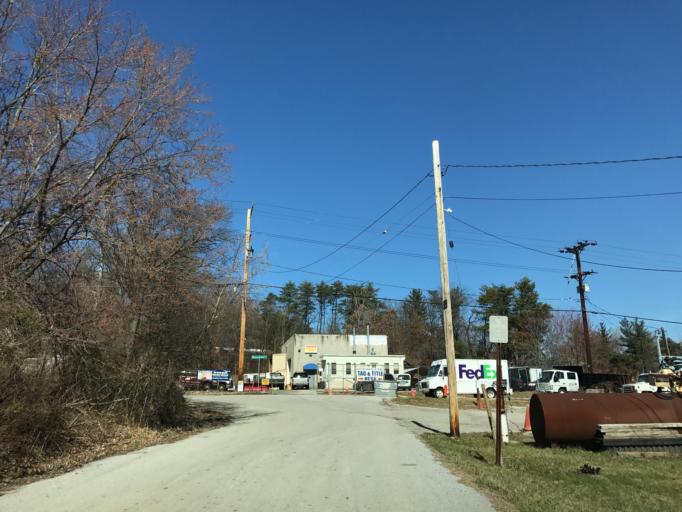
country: US
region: Maryland
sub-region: Baltimore County
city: Lansdowne
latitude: 39.2371
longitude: -76.6687
